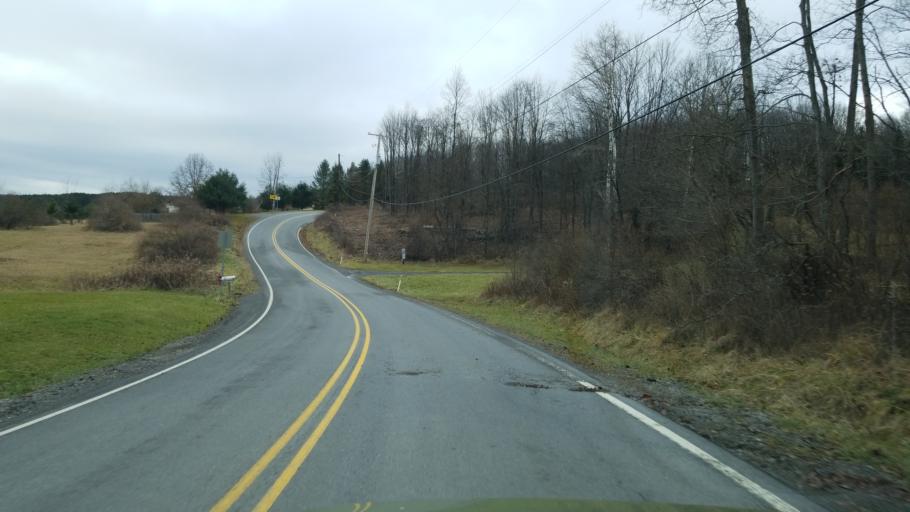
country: US
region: Pennsylvania
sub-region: Clearfield County
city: Hyde
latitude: 41.0340
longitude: -78.4784
